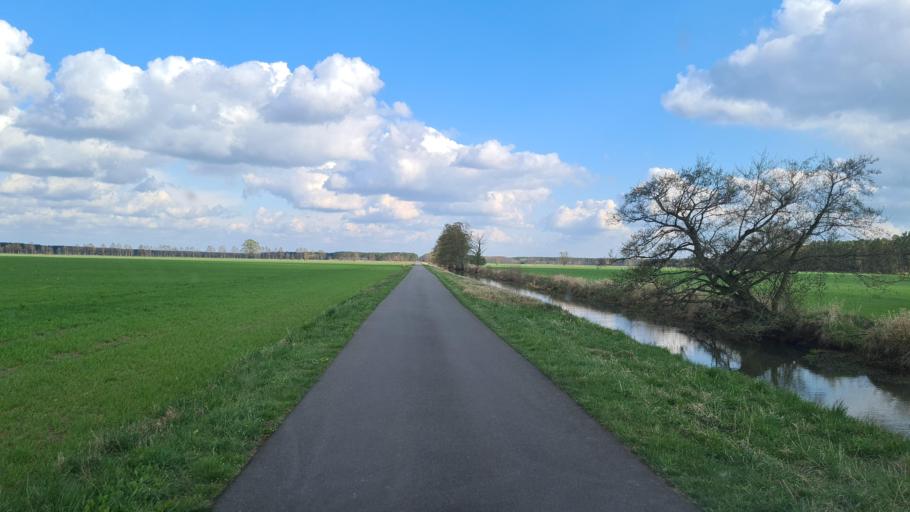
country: DE
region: Brandenburg
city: Herzberg
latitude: 51.7483
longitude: 13.2086
